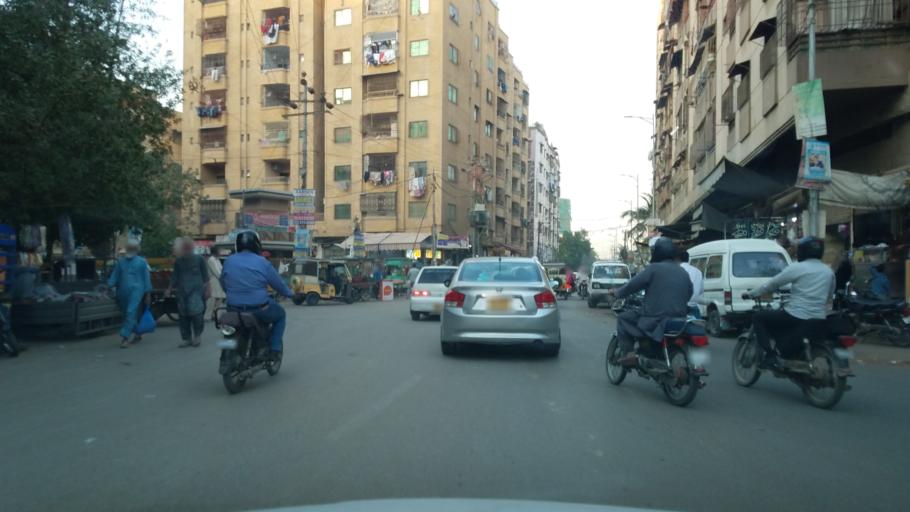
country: PK
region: Sindh
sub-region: Karachi District
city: Karachi
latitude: 24.8788
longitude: 67.0202
